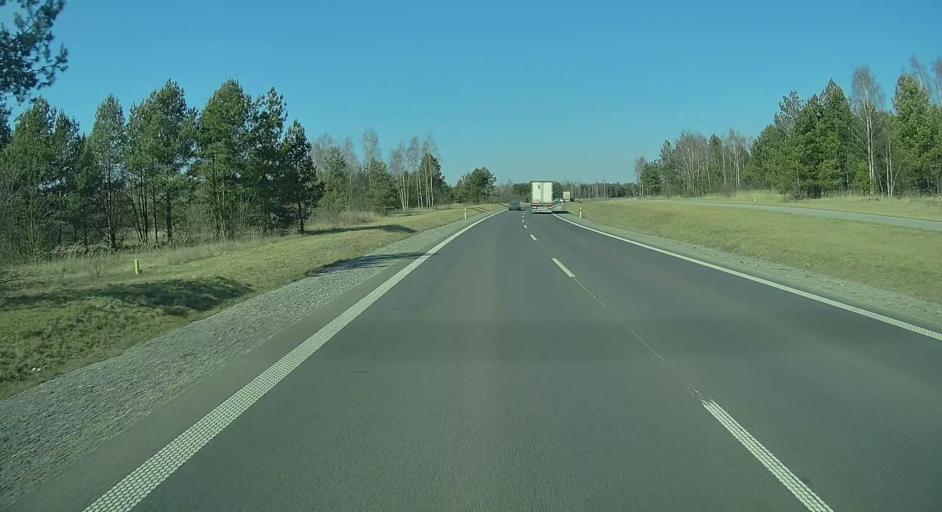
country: PL
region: Subcarpathian Voivodeship
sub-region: Powiat nizanski
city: Raclawice
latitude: 50.4966
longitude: 22.1818
